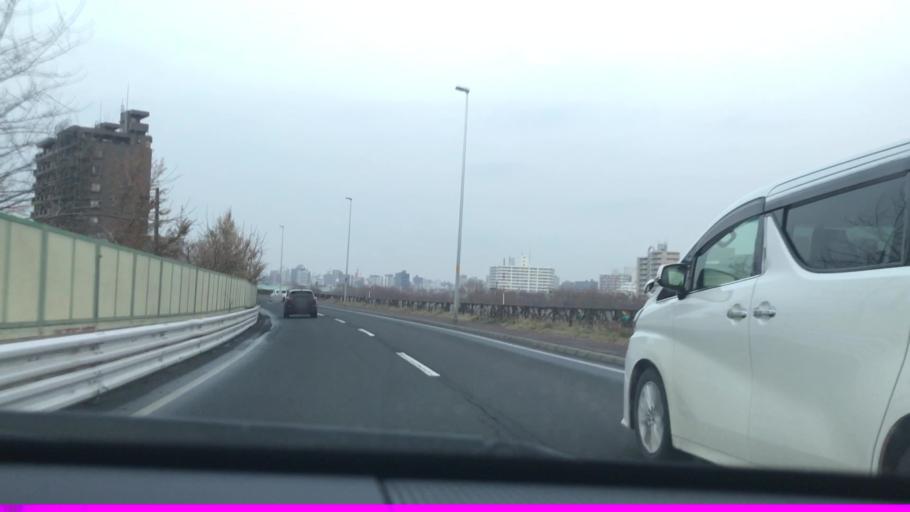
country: JP
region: Hokkaido
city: Sapporo
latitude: 43.0229
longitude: 141.3511
